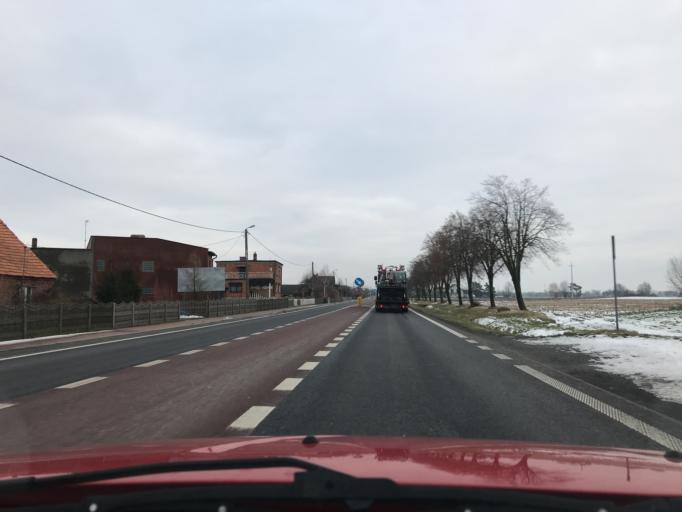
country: PL
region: Greater Poland Voivodeship
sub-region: Powiat pleszewski
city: Goluchow
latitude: 51.8698
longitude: 17.8955
